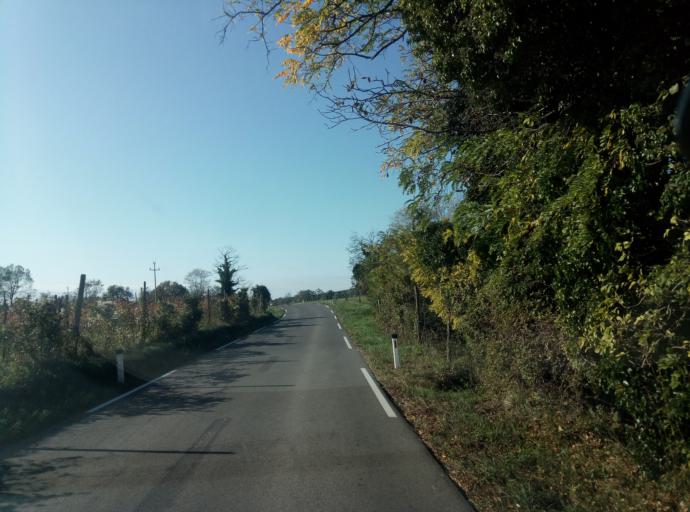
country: SI
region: Komen
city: Komen
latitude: 45.8143
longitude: 13.7399
